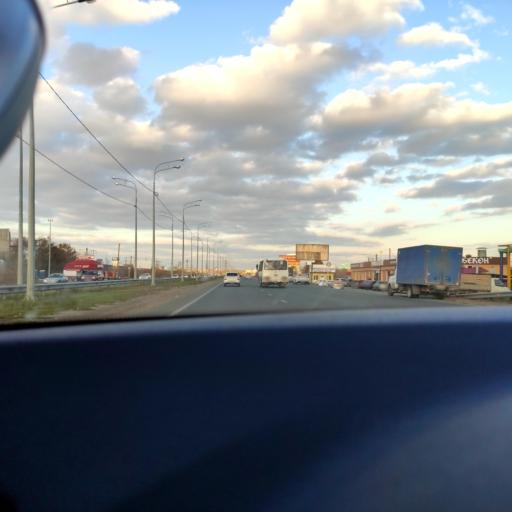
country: RU
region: Samara
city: Smyshlyayevka
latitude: 53.2606
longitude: 50.3794
